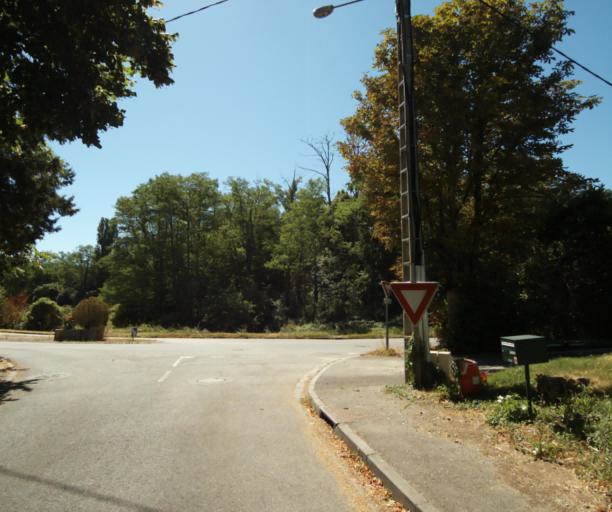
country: FR
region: Midi-Pyrenees
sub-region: Departement de la Haute-Garonne
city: Castanet-Tolosan
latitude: 43.5152
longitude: 1.4862
